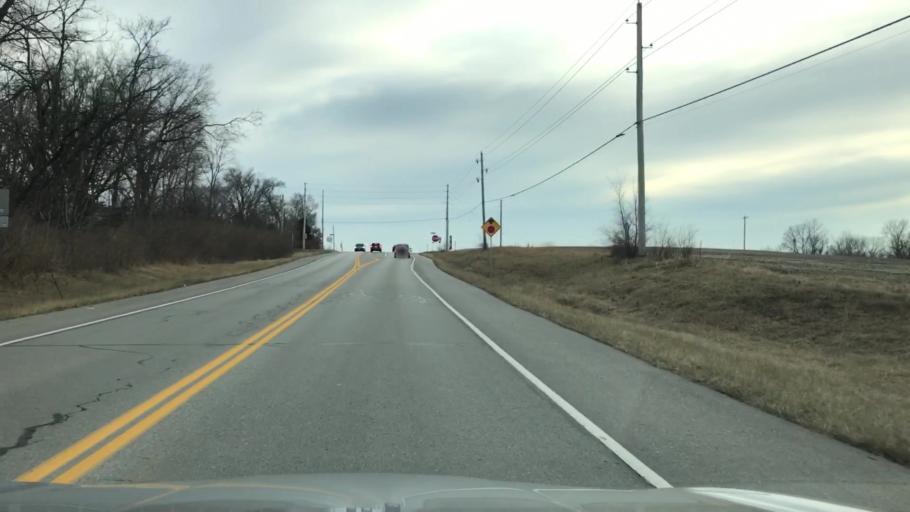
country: US
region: Missouri
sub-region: Jackson County
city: Lees Summit
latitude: 38.8916
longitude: -94.4148
